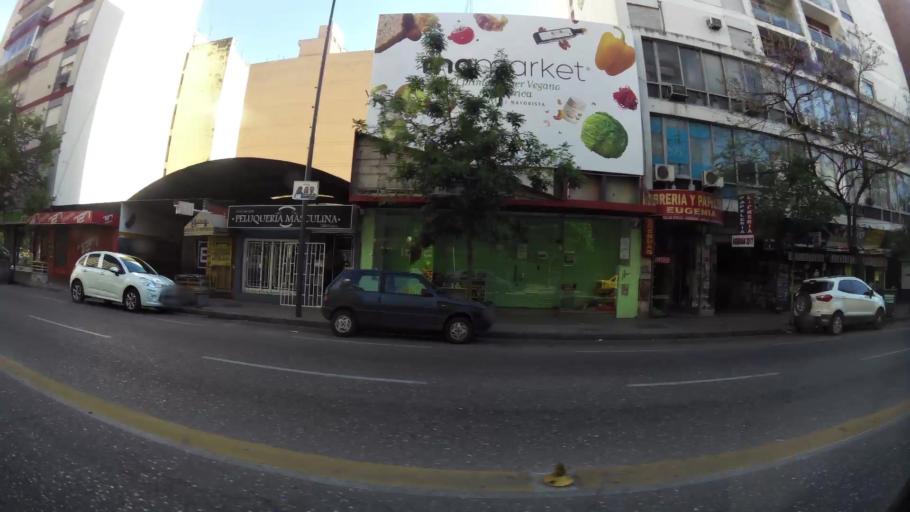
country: AR
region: Cordoba
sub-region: Departamento de Capital
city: Cordoba
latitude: -31.4122
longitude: -64.1878
